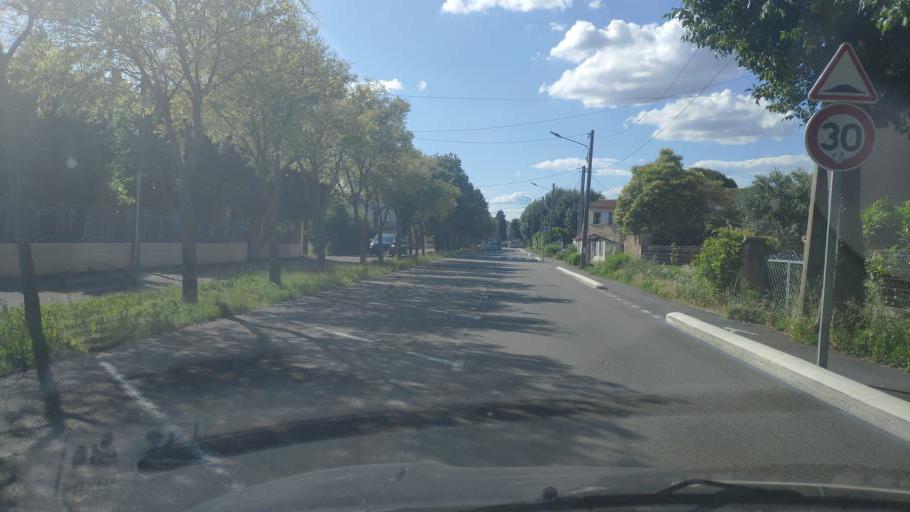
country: FR
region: Provence-Alpes-Cote d'Azur
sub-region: Departement du Vaucluse
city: Entraigues-sur-la-Sorgue
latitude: 44.0022
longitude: 4.9303
